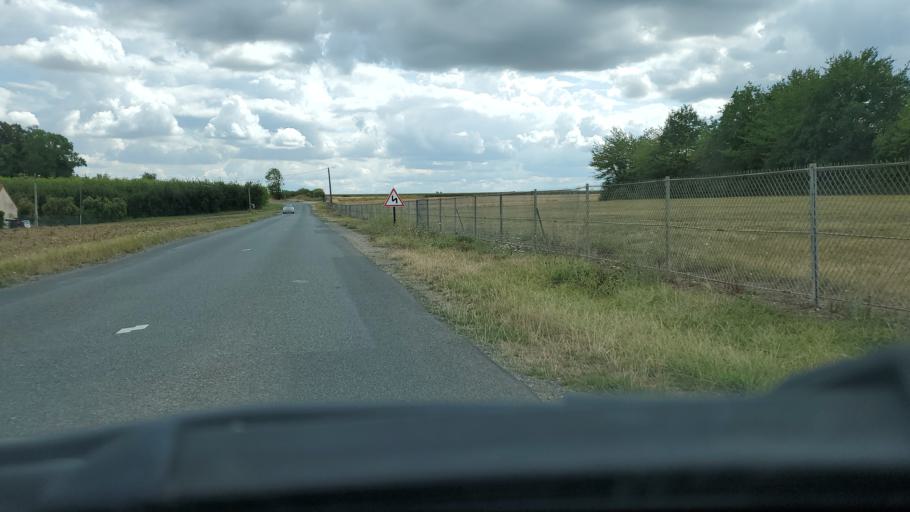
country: FR
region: Ile-de-France
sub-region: Departement de Seine-et-Marne
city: Pommeuse
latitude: 48.8454
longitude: 3.0187
